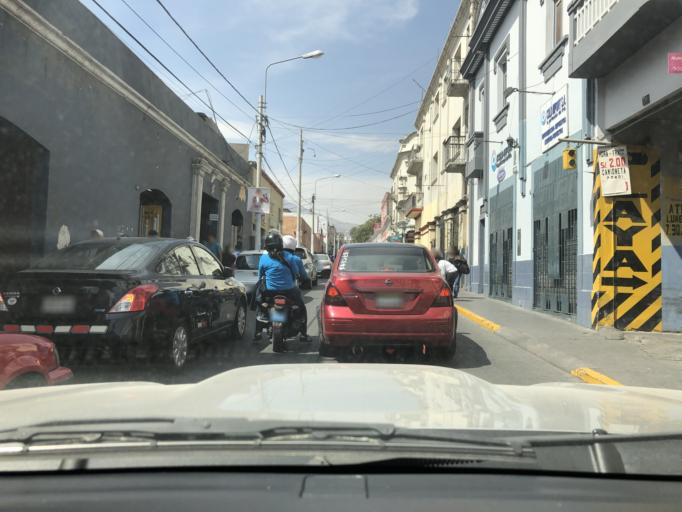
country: PE
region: Arequipa
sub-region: Provincia de Arequipa
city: Arequipa
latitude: -16.4015
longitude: -71.5325
